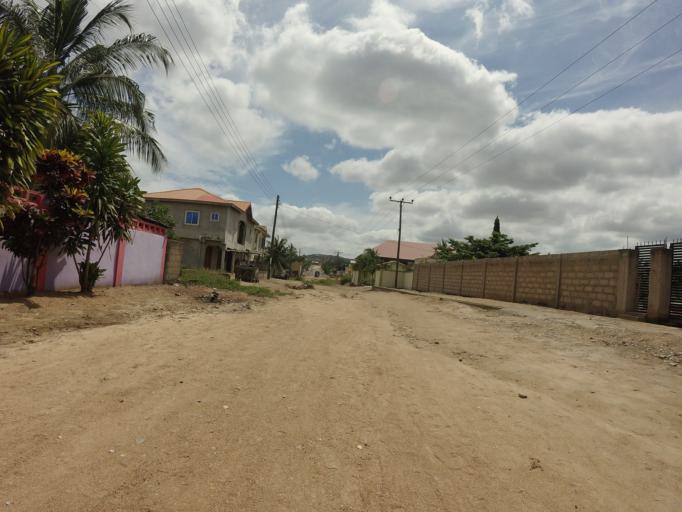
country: GH
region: Central
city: Kasoa
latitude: 5.5459
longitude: -0.4010
